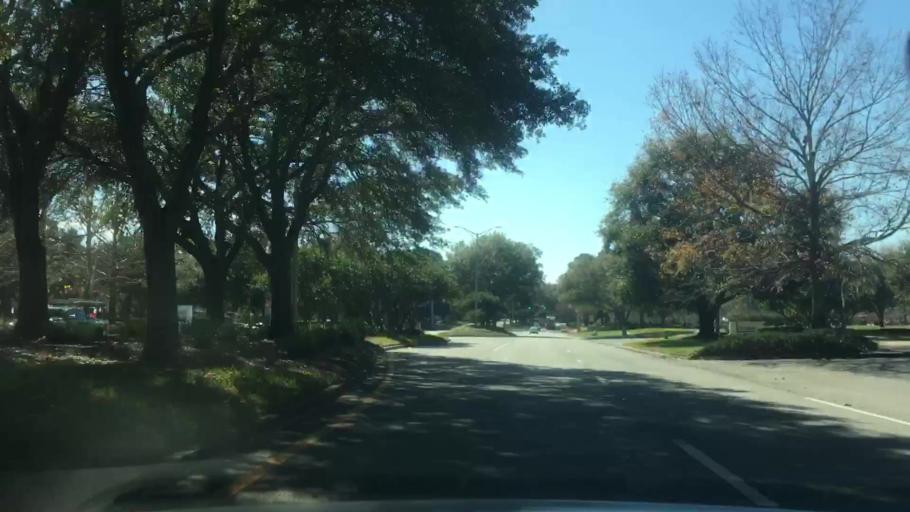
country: US
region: Florida
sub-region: Duval County
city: Jacksonville
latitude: 30.2426
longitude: -81.5455
